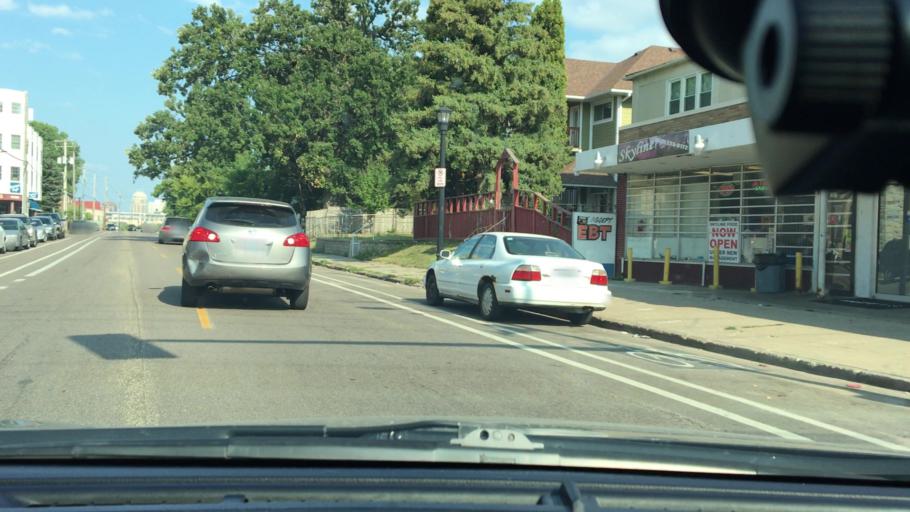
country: US
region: Minnesota
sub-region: Hennepin County
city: Minneapolis
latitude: 44.9808
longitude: -93.3045
